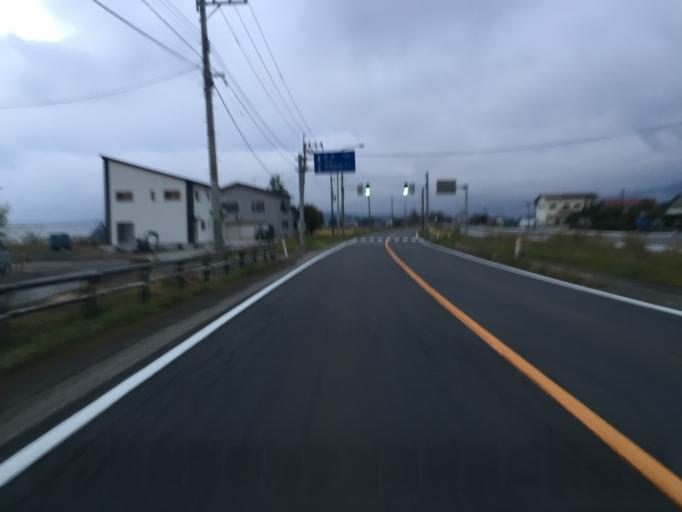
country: JP
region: Fukushima
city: Inawashiro
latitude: 37.5359
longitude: 140.0988
